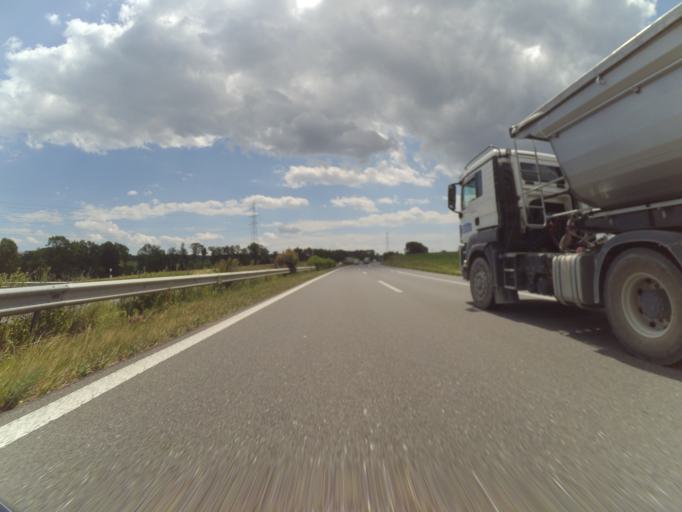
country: CH
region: Vaud
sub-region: Jura-Nord vaudois District
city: Chavornay
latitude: 46.7103
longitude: 6.5793
